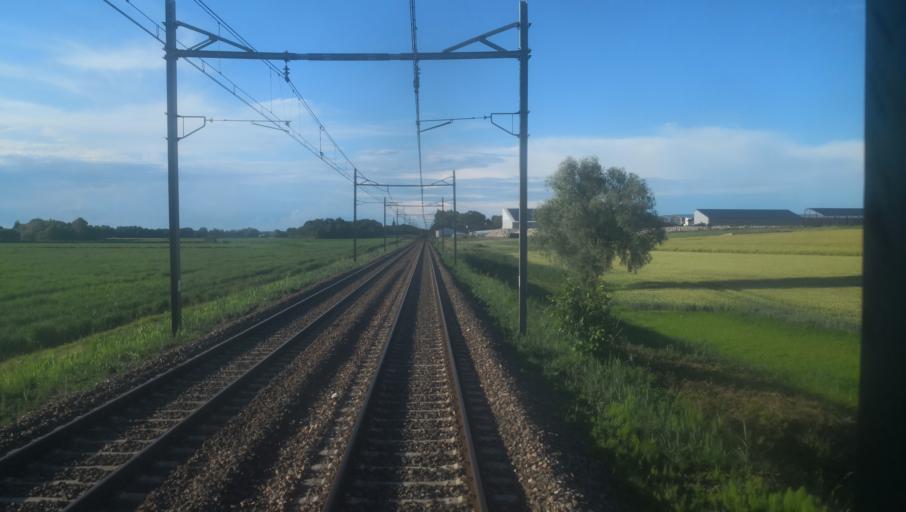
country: FR
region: Centre
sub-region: Departement du Cher
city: Mereau
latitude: 47.1389
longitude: 2.0469
